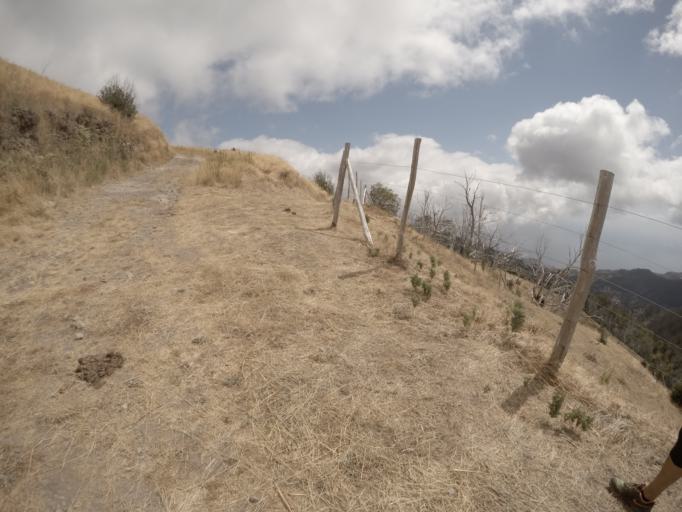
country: PT
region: Madeira
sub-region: Camara de Lobos
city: Curral das Freiras
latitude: 32.7090
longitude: -16.9988
